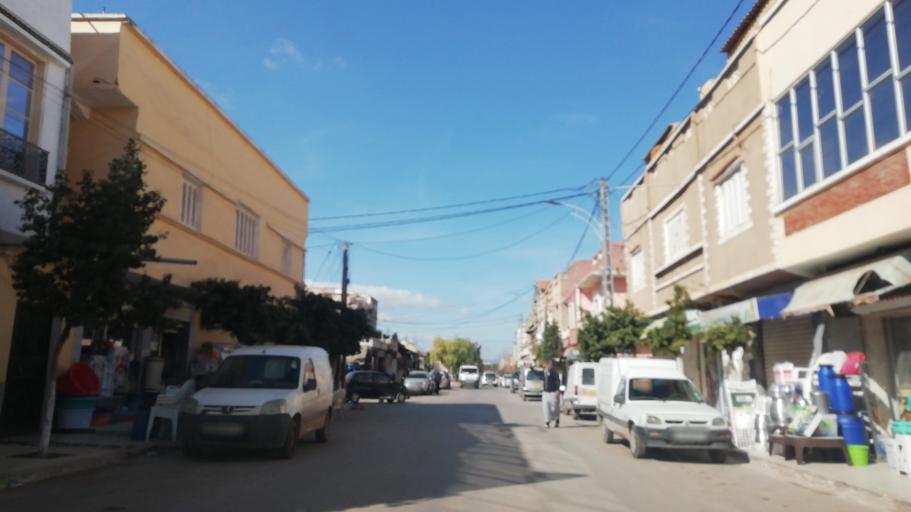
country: DZ
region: Oran
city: Es Senia
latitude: 35.6143
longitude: -0.5787
